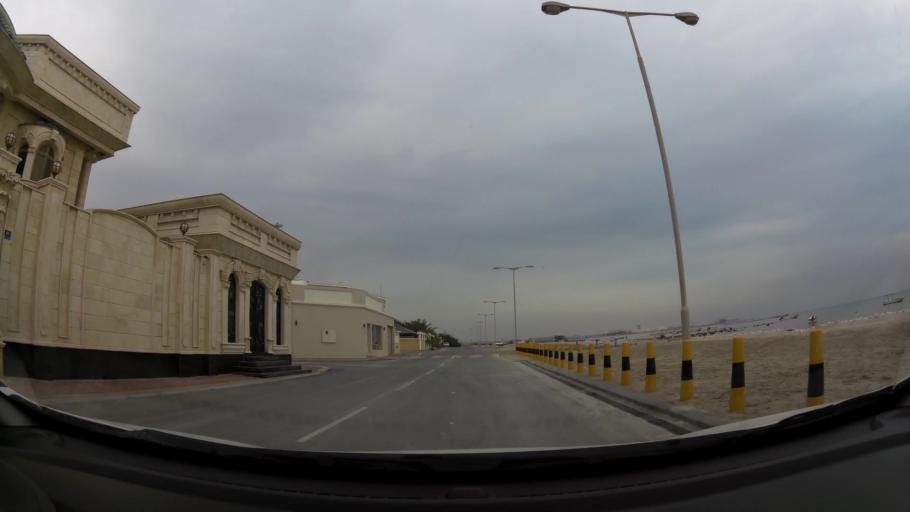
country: BH
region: Northern
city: Ar Rifa'
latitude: 26.0587
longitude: 50.6186
